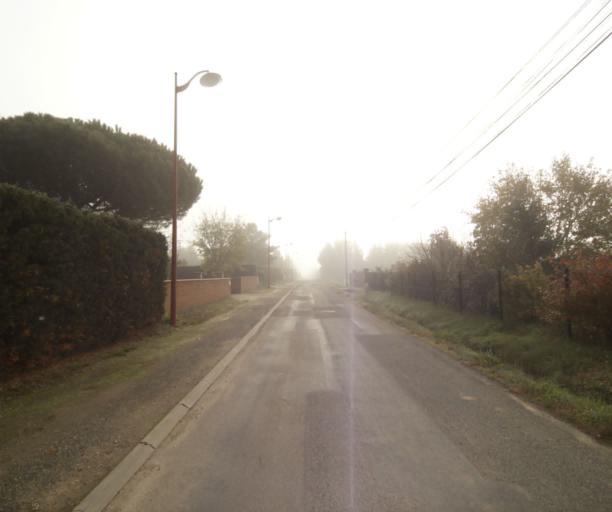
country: FR
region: Midi-Pyrenees
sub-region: Departement du Tarn-et-Garonne
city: Nohic
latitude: 43.8884
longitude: 1.4411
